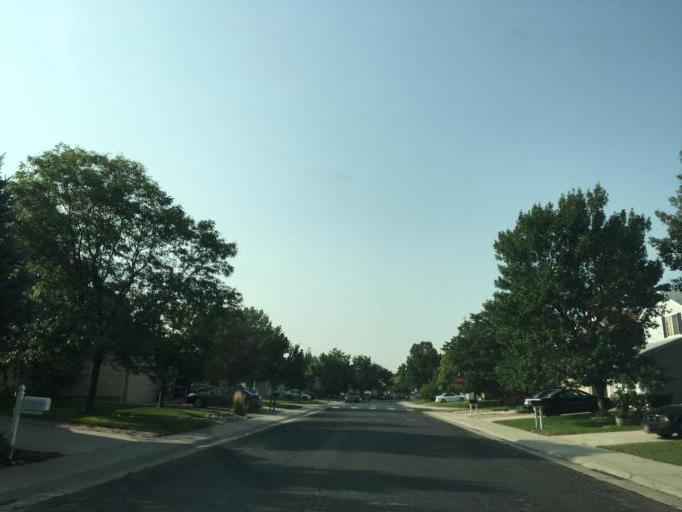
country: US
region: Colorado
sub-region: Adams County
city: Todd Creek
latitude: 39.9068
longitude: -104.8534
